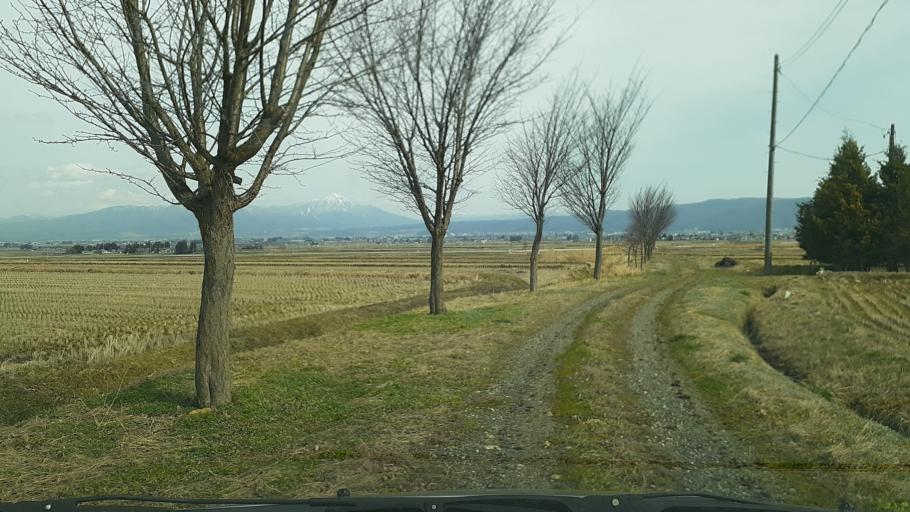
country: JP
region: Fukushima
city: Kitakata
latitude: 37.4671
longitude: 139.8184
